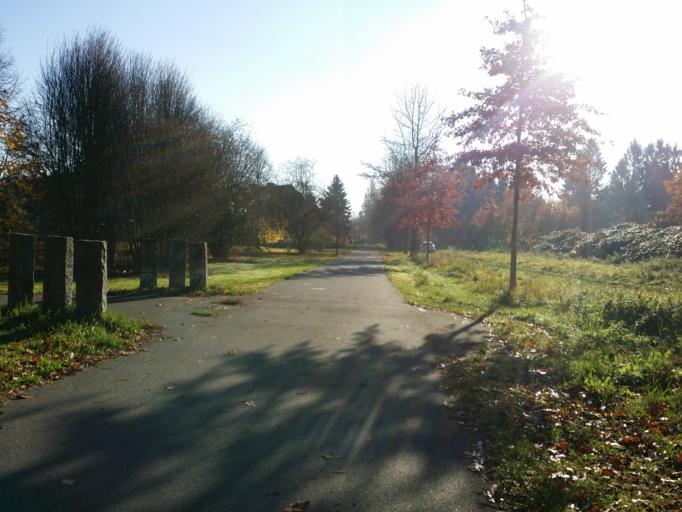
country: DE
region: Bremen
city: Bremen
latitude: 53.0684
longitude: 8.8782
